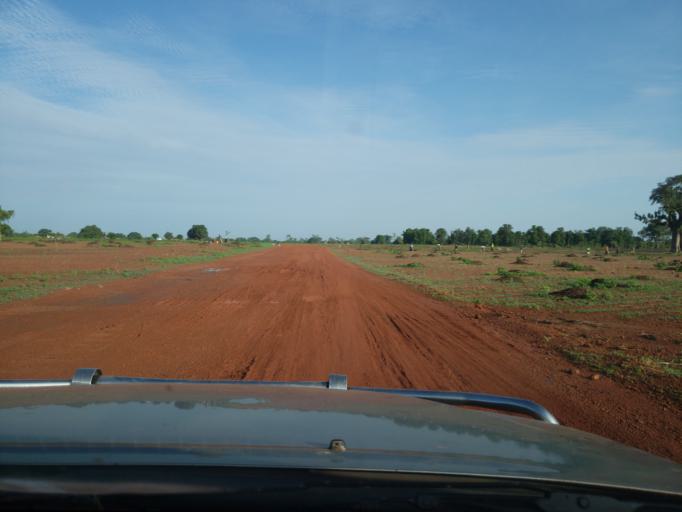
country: ML
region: Sikasso
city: Koutiala
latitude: 12.4292
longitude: -5.6051
